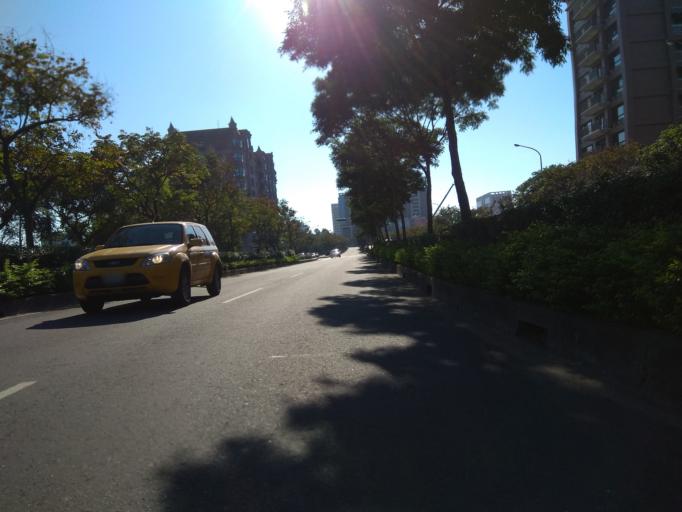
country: TW
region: Taiwan
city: Taoyuan City
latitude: 25.0186
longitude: 121.2245
